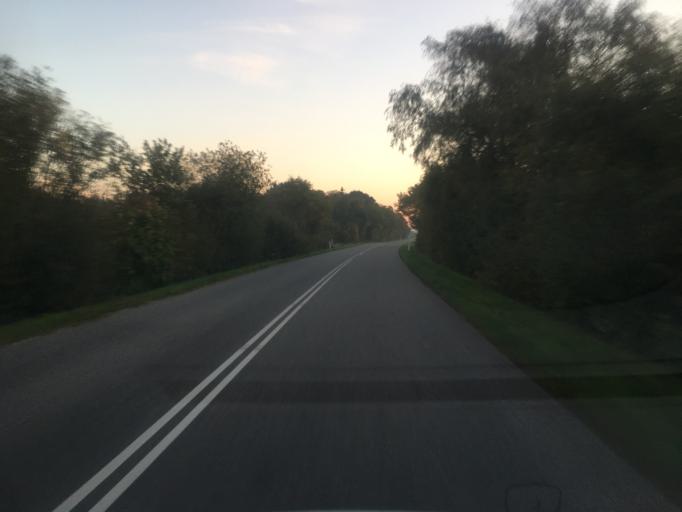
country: DE
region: Schleswig-Holstein
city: Bramstedtlund
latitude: 54.9694
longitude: 9.1224
